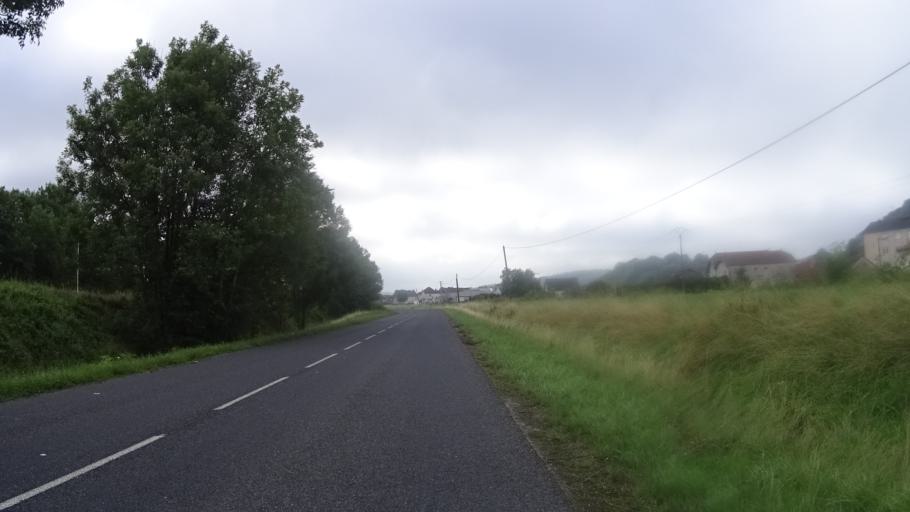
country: FR
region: Lorraine
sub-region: Departement de la Meuse
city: Fains-Veel
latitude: 48.7946
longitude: 5.1209
